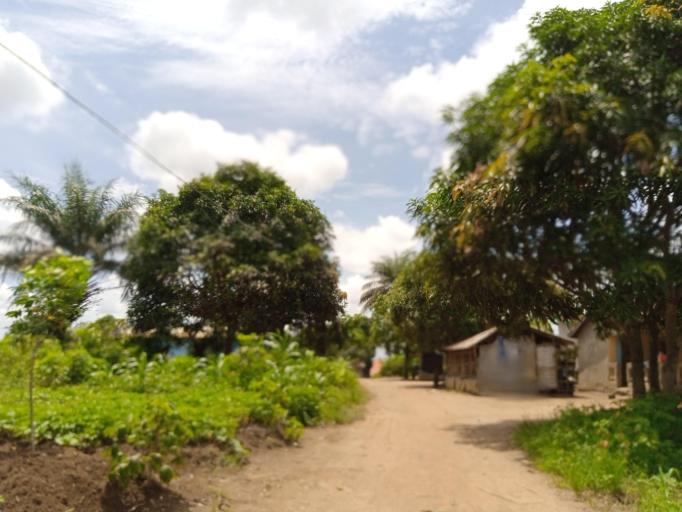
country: SL
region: Northern Province
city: Masoyila
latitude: 8.5949
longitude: -13.1831
